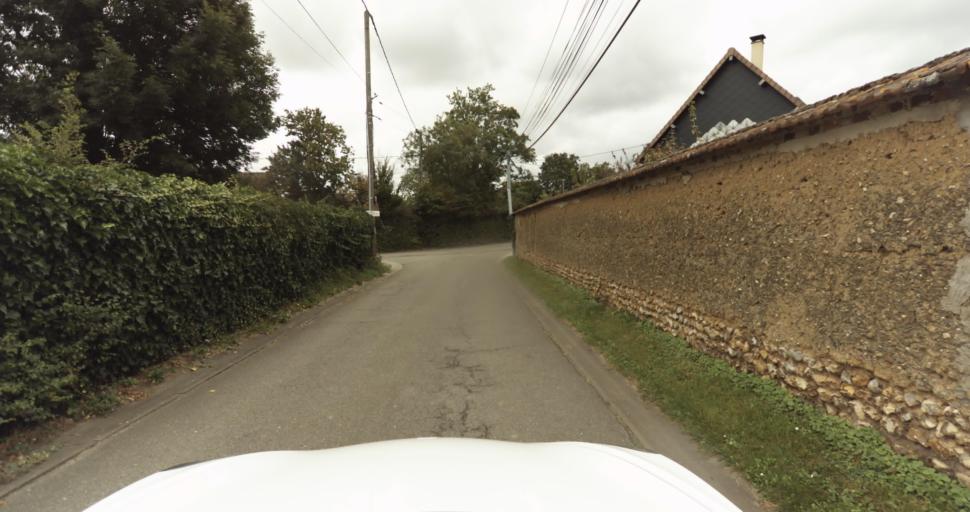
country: FR
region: Haute-Normandie
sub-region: Departement de l'Eure
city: Saint-Sebastien-de-Morsent
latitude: 49.0113
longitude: 1.0654
